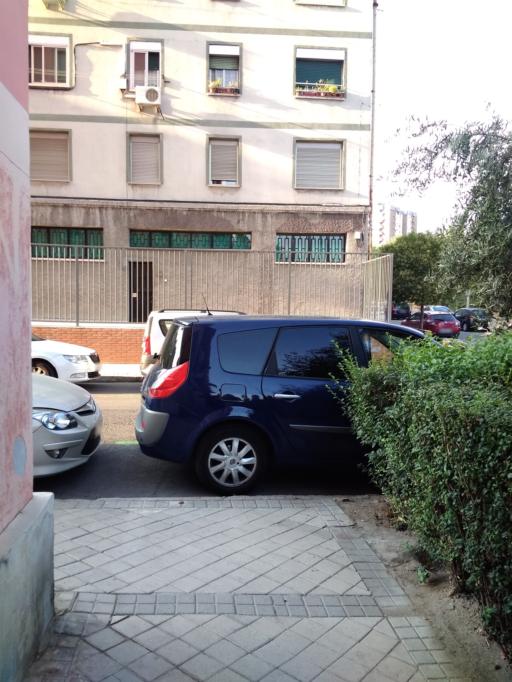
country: ES
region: Madrid
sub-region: Provincia de Madrid
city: Puente de Vallecas
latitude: 40.4072
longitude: -3.6660
